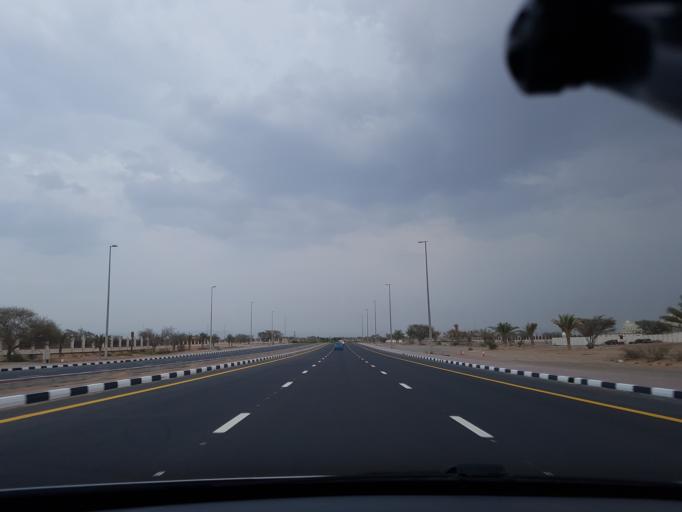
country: AE
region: Ash Shariqah
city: Adh Dhayd
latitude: 25.2675
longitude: 55.9080
